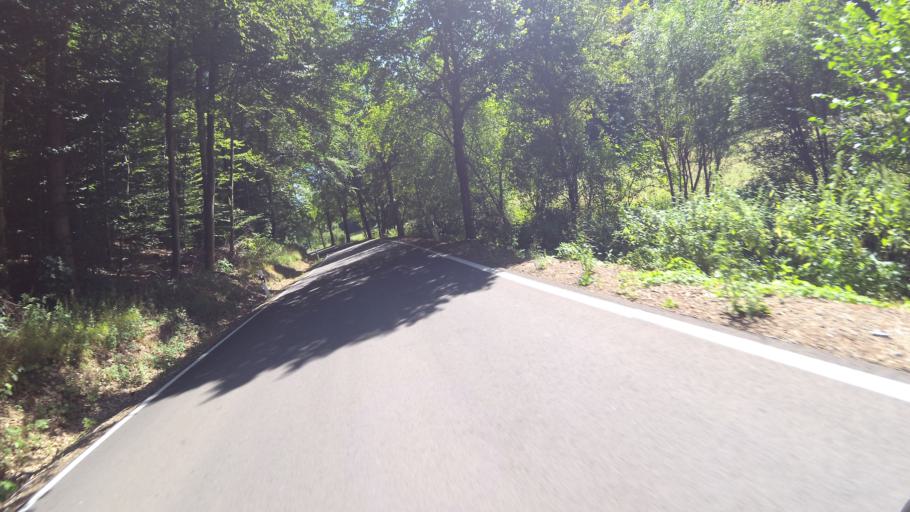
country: DE
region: Rheinland-Pfalz
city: Zweibrucken
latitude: 49.2525
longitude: 7.3123
